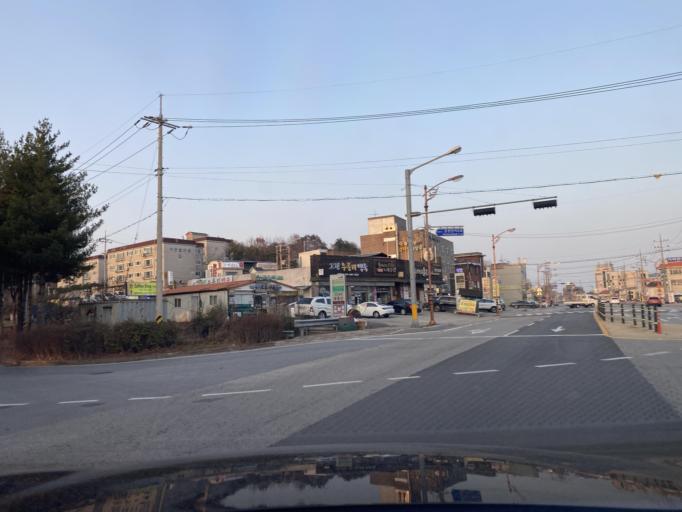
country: KR
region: Chungcheongnam-do
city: Hongsung
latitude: 36.6930
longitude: 126.6602
